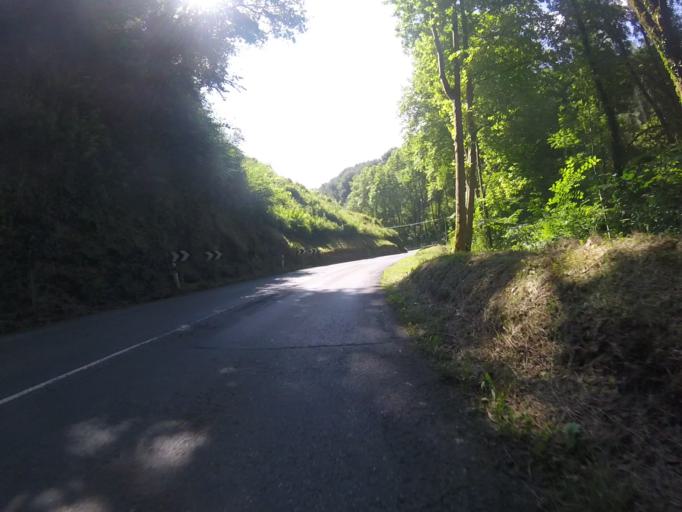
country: ES
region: Basque Country
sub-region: Provincia de Guipuzcoa
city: Errezil
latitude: 43.1749
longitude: -2.2111
